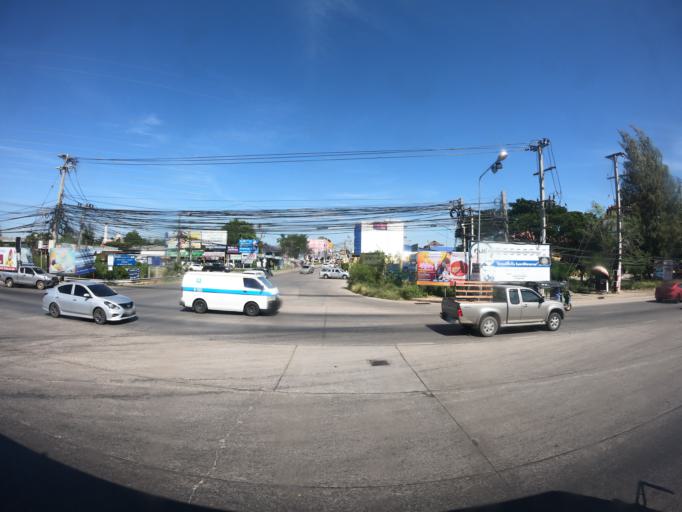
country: TH
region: Nakhon Ratchasima
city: Nakhon Ratchasima
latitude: 14.9954
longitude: 102.1038
